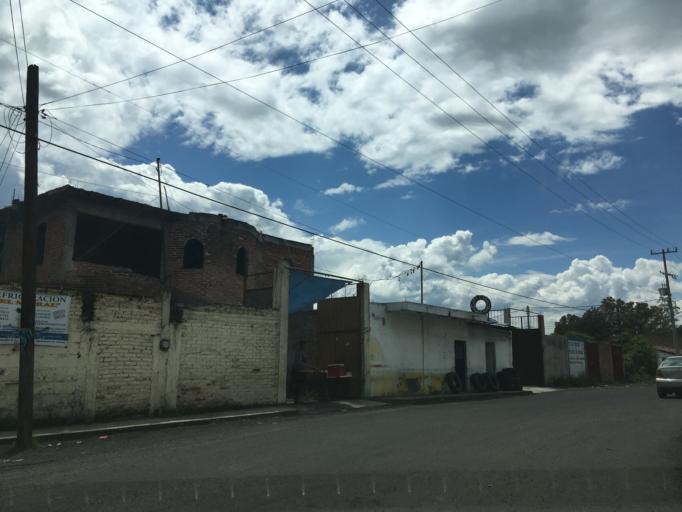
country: MX
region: Michoacan
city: Zacapu
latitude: 19.8350
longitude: -101.7284
